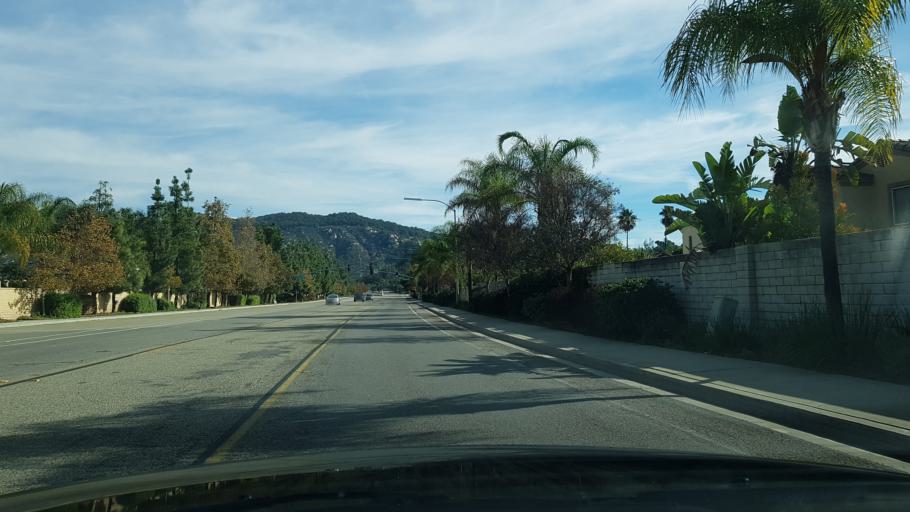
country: US
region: California
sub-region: San Diego County
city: Escondido
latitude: 33.1502
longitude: -117.0409
